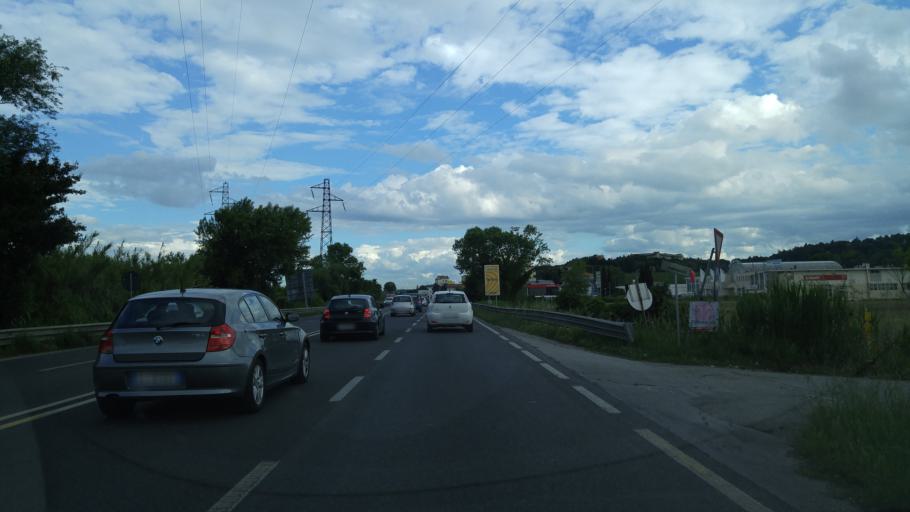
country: IT
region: Emilia-Romagna
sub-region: Provincia di Rimini
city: Rimini
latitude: 44.0504
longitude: 12.5481
